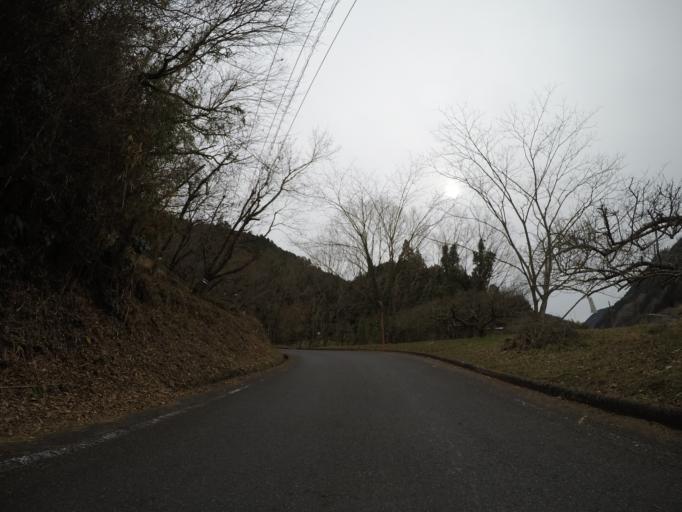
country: JP
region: Shizuoka
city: Fujinomiya
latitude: 35.2586
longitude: 138.5335
